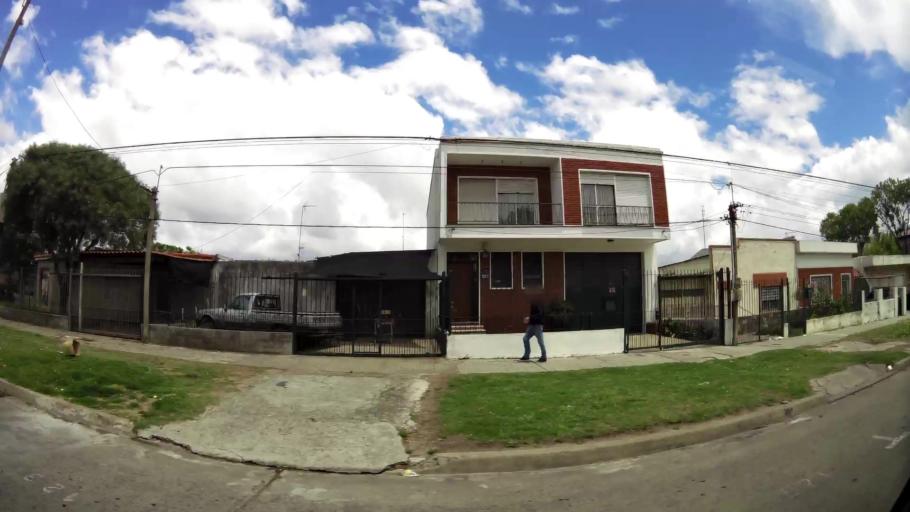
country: UY
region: Montevideo
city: Montevideo
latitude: -34.8701
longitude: -56.1422
